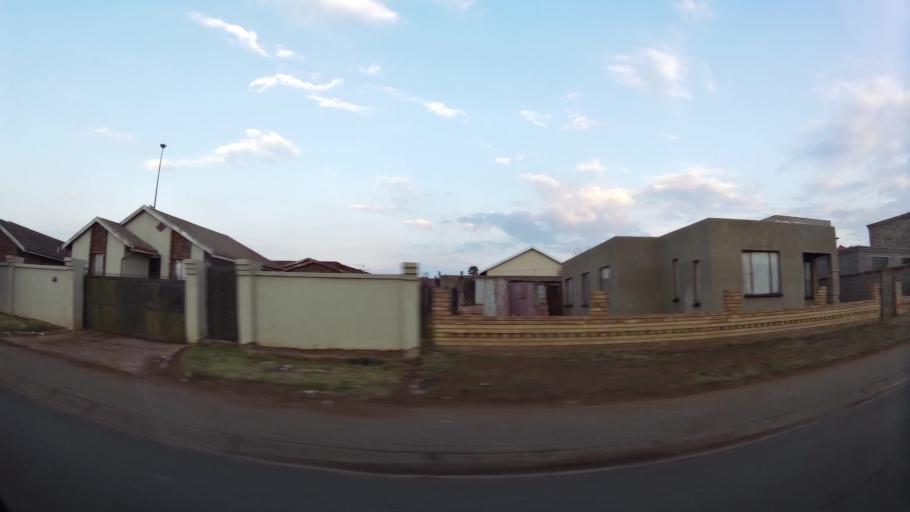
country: ZA
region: Gauteng
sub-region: City of Johannesburg Metropolitan Municipality
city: Orange Farm
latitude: -26.5600
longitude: 27.8552
